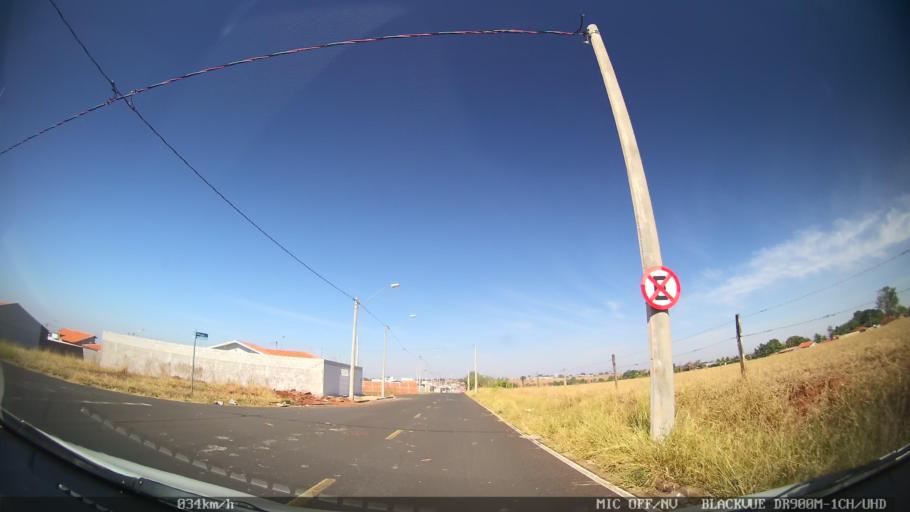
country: BR
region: Sao Paulo
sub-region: Sao Jose Do Rio Preto
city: Sao Jose do Rio Preto
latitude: -20.7566
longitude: -49.4241
